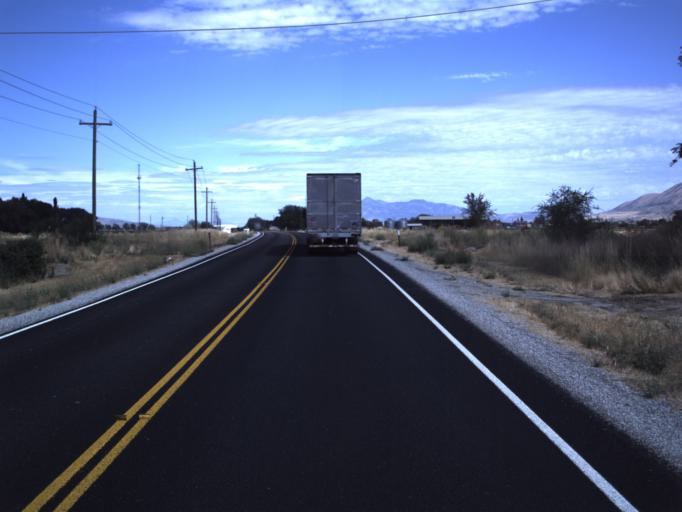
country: US
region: Utah
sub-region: Box Elder County
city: Honeyville
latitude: 41.6290
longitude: -112.1270
